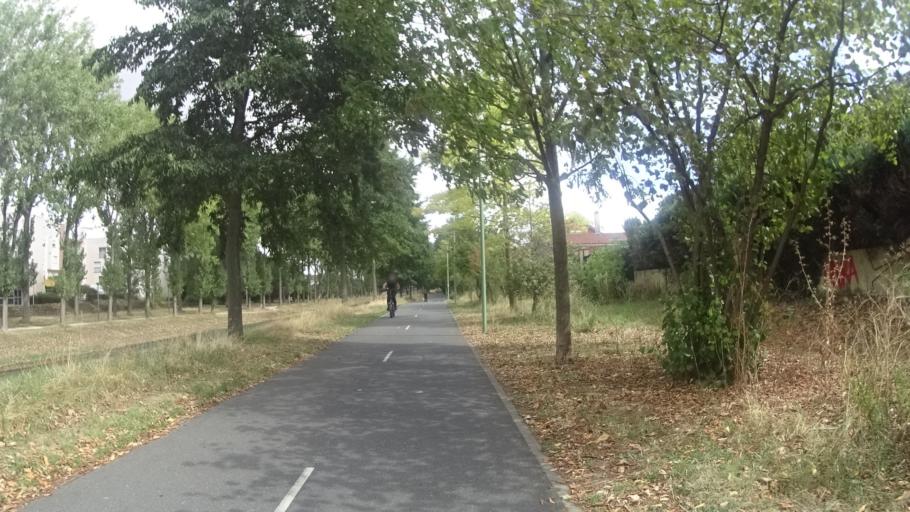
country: FR
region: Ile-de-France
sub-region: Departement de Seine-Saint-Denis
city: Les Pavillons-sous-Bois
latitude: 48.9220
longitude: 2.5106
